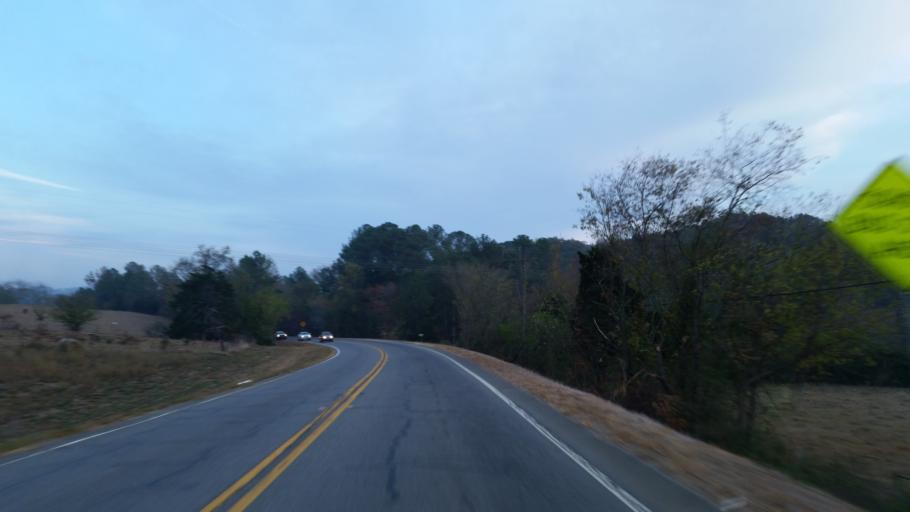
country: US
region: Georgia
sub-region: Murray County
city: Chatsworth
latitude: 34.5878
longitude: -84.7195
